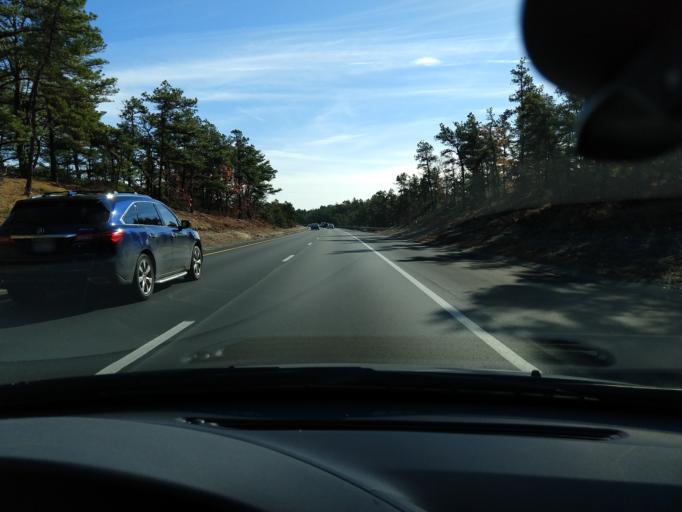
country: US
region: Massachusetts
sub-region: Plymouth County
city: White Island Shores
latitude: 41.8804
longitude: -70.6085
